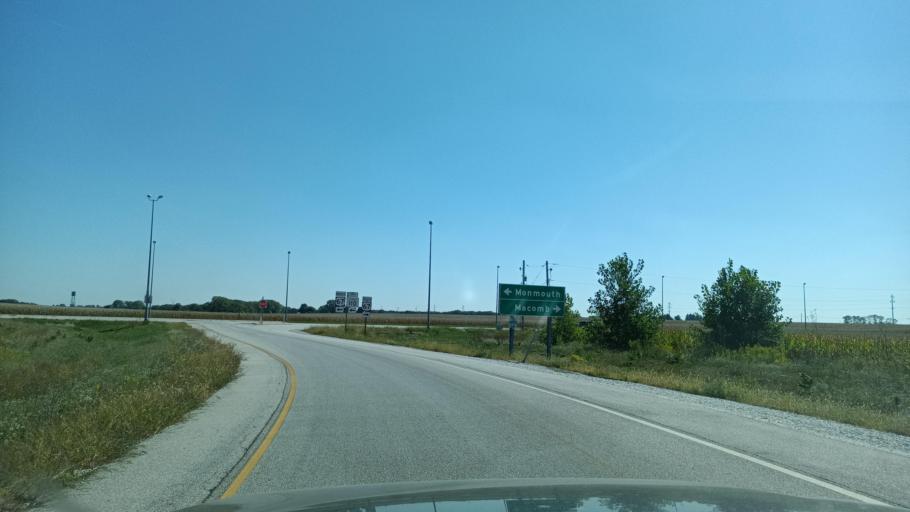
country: US
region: Illinois
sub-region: McDonough County
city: Macomb
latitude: 40.5019
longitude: -90.6758
